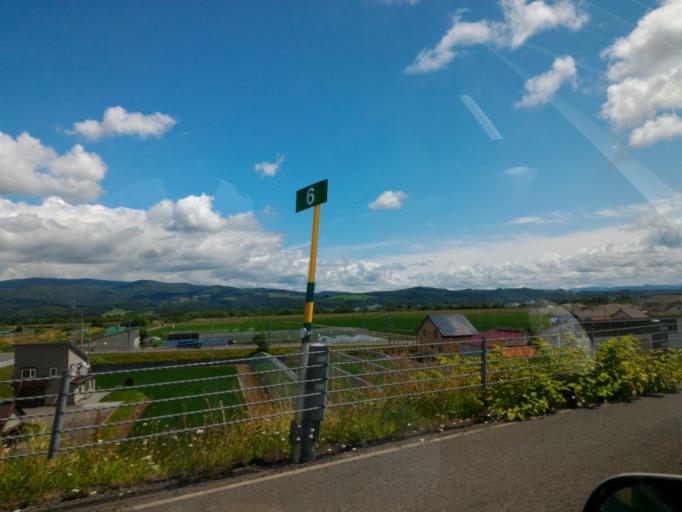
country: JP
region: Hokkaido
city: Nayoro
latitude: 44.3709
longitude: 142.4341
